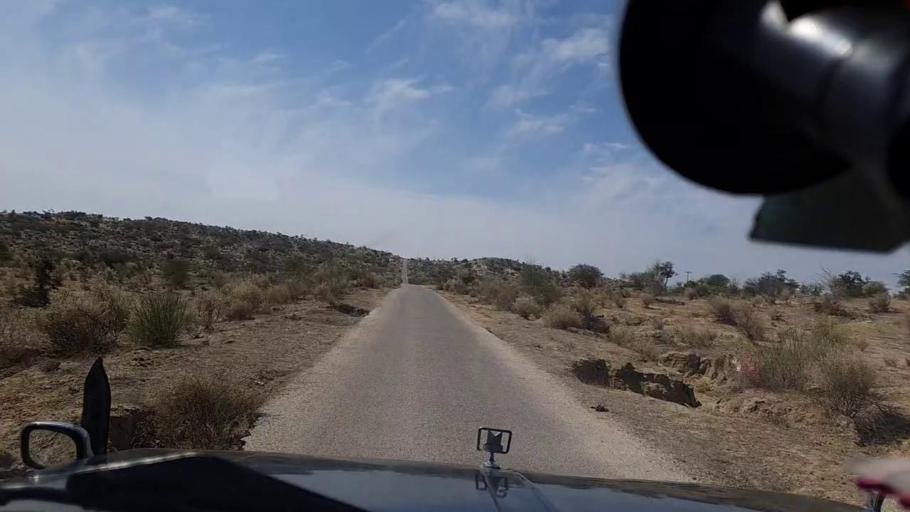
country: PK
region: Sindh
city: Diplo
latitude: 24.3894
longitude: 69.5887
